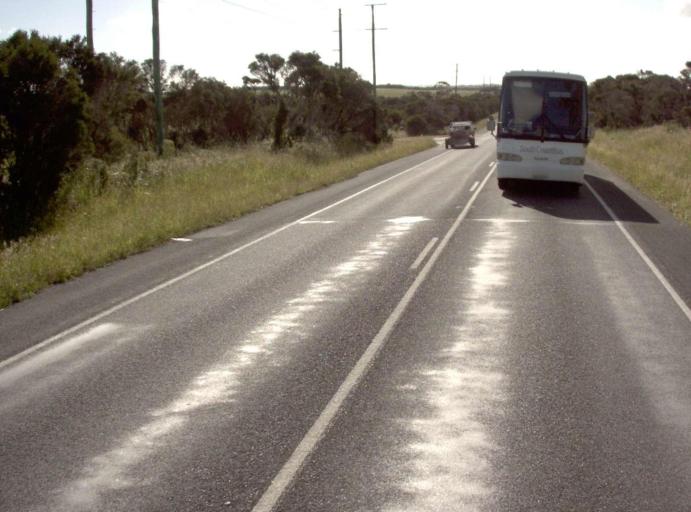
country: AU
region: Victoria
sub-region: Bass Coast
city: North Wonthaggi
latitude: -38.6162
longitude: 145.6561
